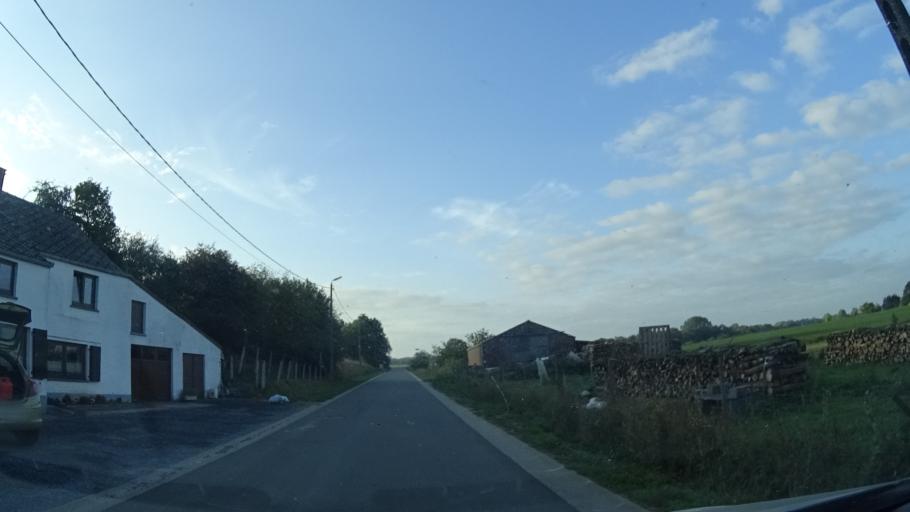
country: BE
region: Wallonia
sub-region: Province de Namur
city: Cerfontaine
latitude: 50.2119
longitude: 4.3589
